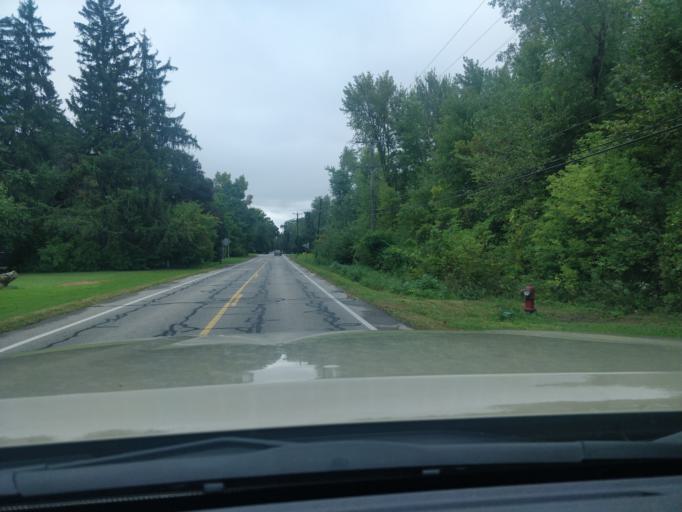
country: US
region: Michigan
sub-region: Wayne County
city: Romulus
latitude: 42.1976
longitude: -83.4237
